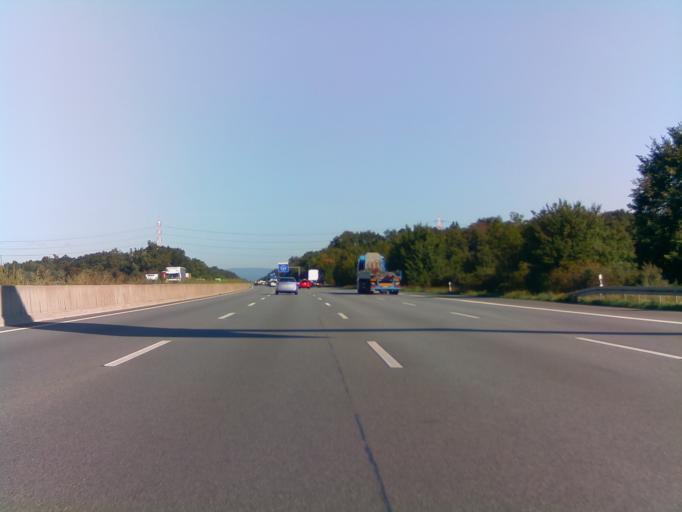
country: DE
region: Hesse
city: Weiterstadt
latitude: 49.9341
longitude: 8.6130
